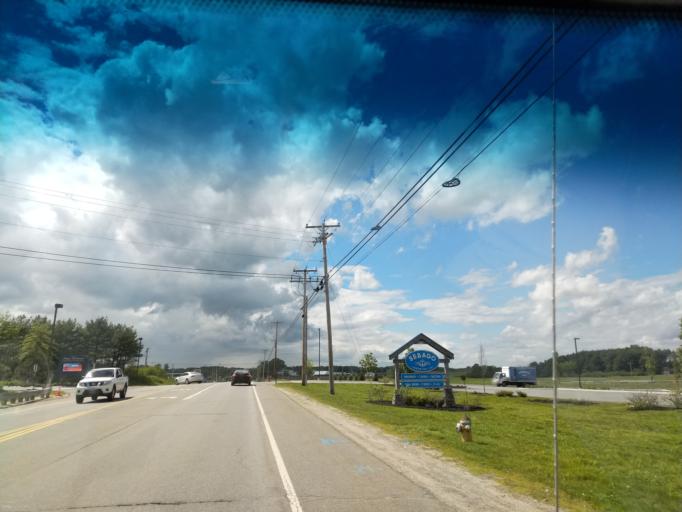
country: US
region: Maine
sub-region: Cumberland County
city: Westbrook
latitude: 43.6883
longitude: -70.3942
